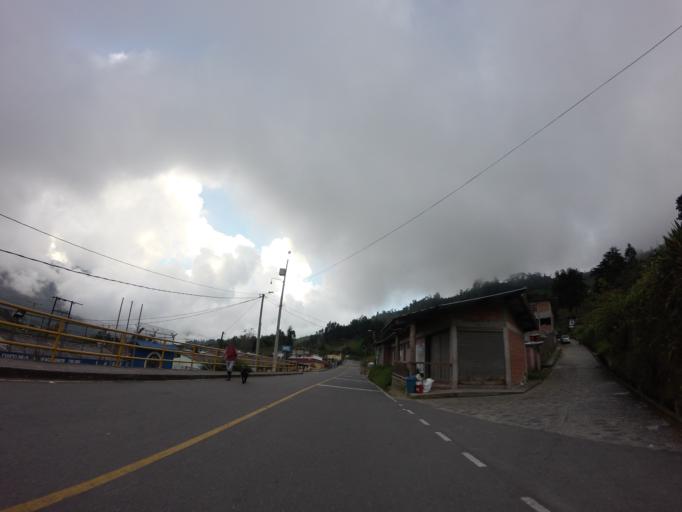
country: CO
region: Caldas
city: Pensilvania
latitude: 5.3783
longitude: -75.1619
